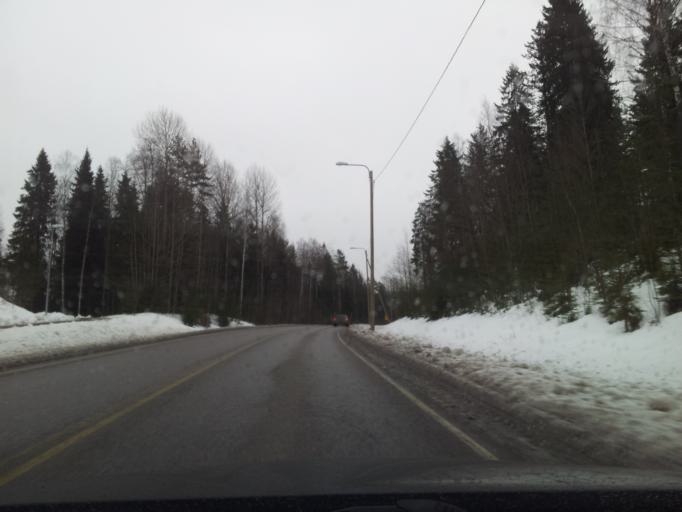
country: FI
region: Uusimaa
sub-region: Helsinki
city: Espoo
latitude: 60.1506
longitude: 24.5534
